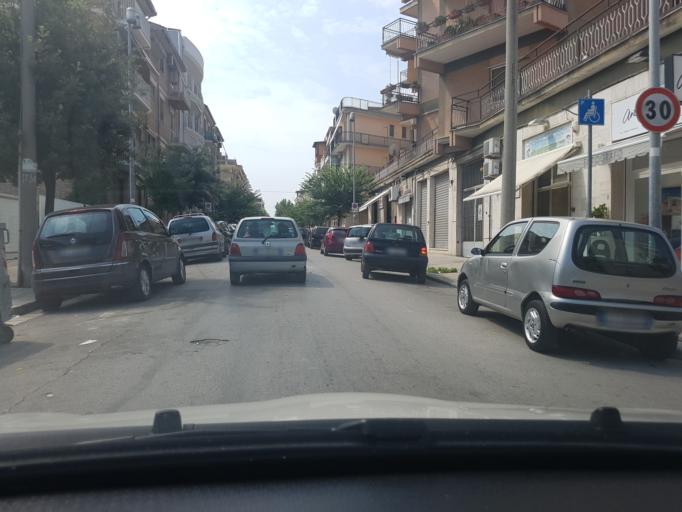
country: IT
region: Apulia
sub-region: Provincia di Foggia
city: Cerignola
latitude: 41.2679
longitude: 15.9039
